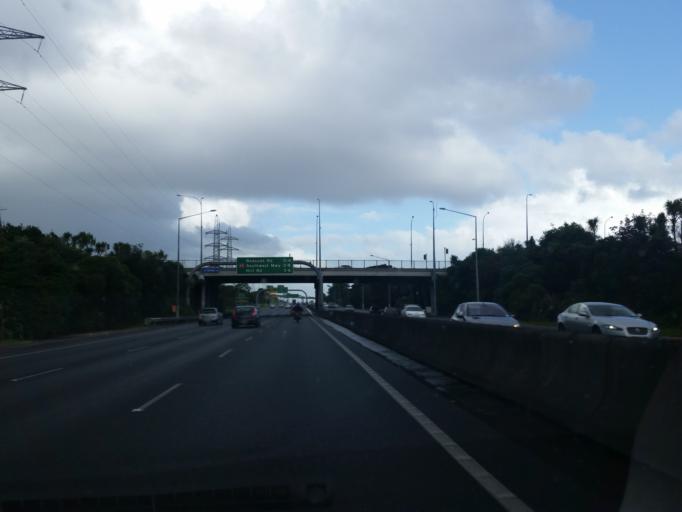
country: NZ
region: Auckland
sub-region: Auckland
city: Manukau City
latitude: -36.9847
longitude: 174.8841
